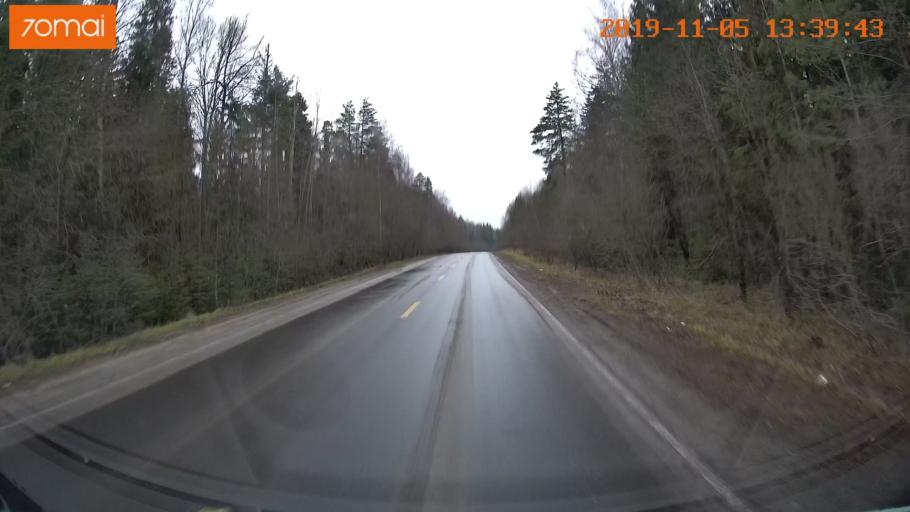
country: RU
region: Ivanovo
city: Shuya
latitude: 56.9423
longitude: 41.3850
